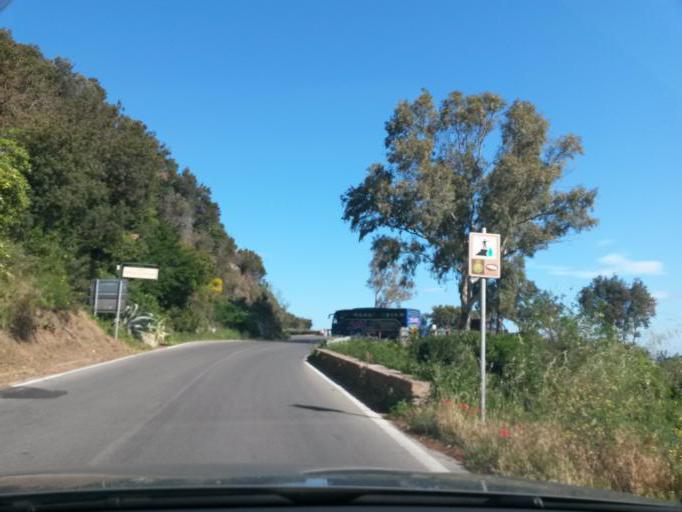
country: IT
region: Tuscany
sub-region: Provincia di Livorno
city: Marciana Marina
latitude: 42.7895
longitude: 10.2270
